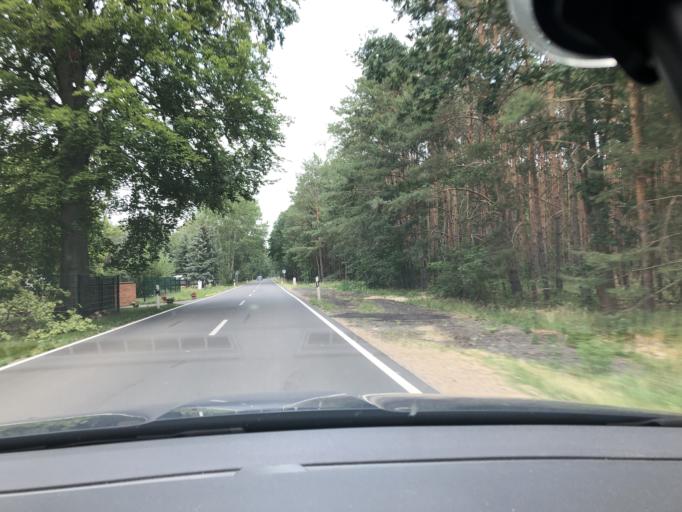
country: DE
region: Brandenburg
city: Kasel-Golzig
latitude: 51.9937
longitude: 13.7809
